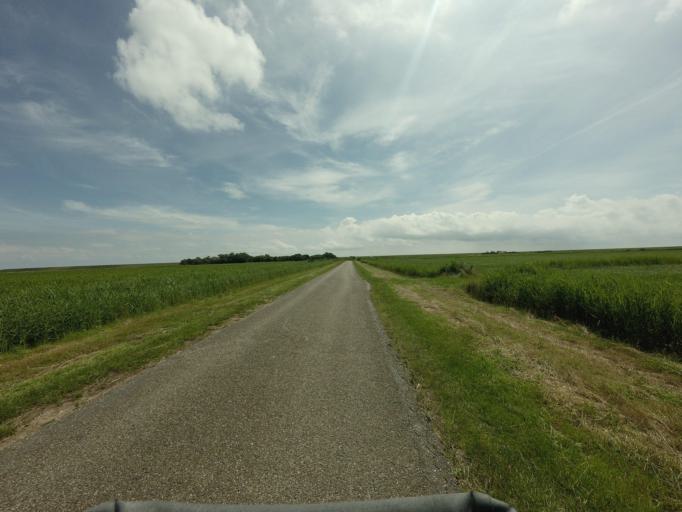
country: NL
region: North Holland
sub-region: Gemeente Texel
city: Den Burg
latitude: 53.0654
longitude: 4.8611
